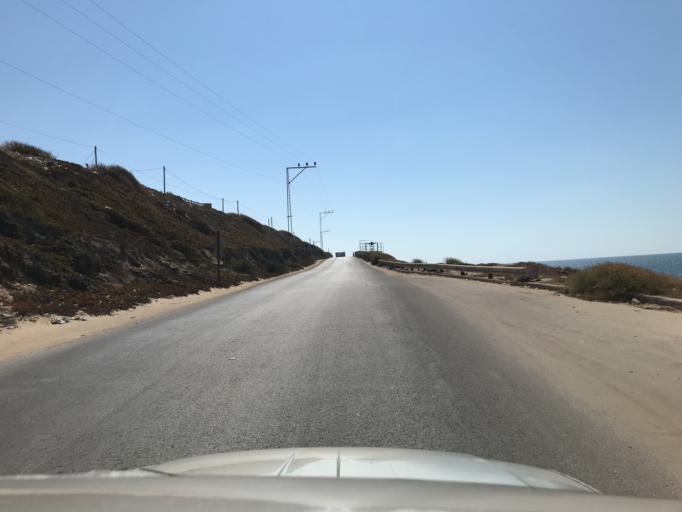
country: PS
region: Gaza Strip
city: An Nusayrat
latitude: 31.4615
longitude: 34.3738
